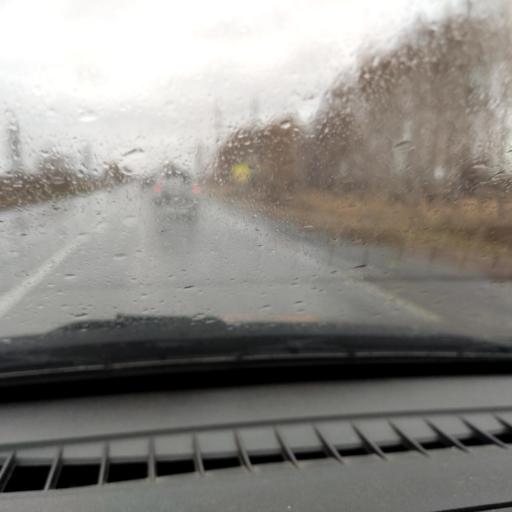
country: RU
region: Samara
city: Tol'yatti
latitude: 53.5847
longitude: 49.3331
